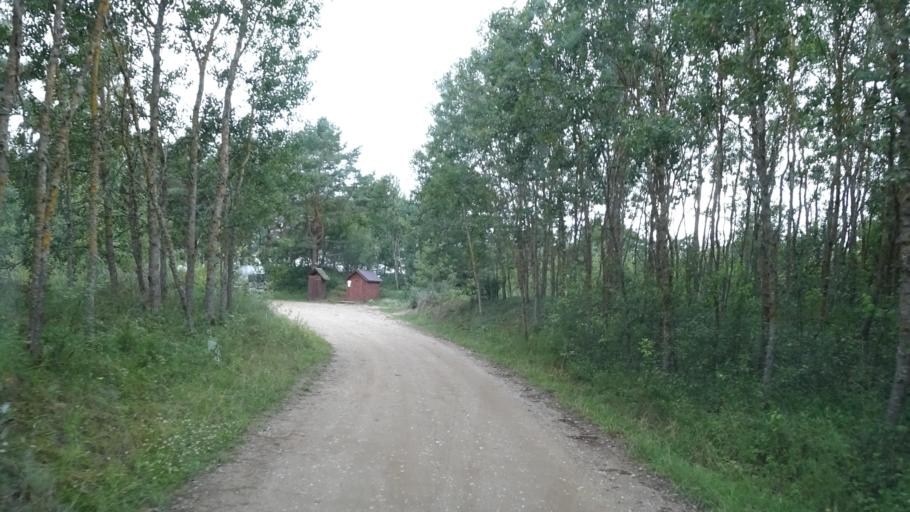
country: LV
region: Liepaja
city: Vec-Liepaja
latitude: 56.6247
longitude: 21.0370
